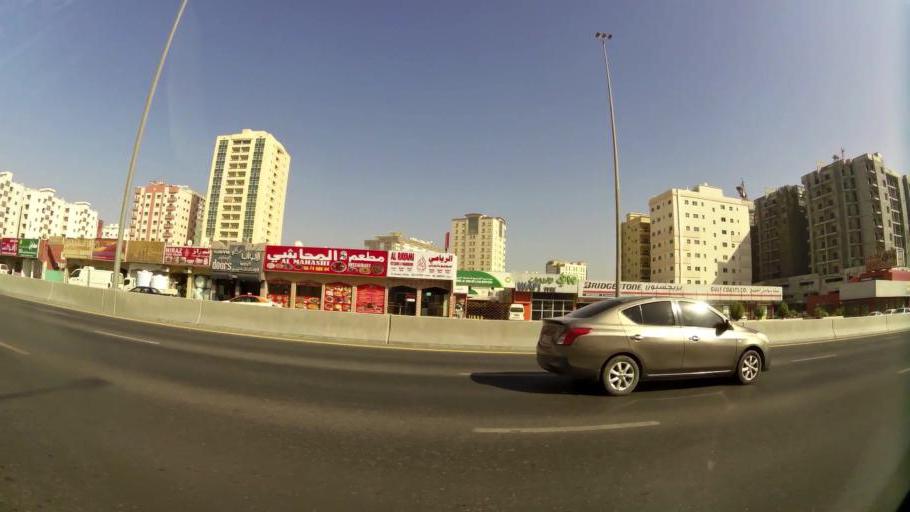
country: AE
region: Ajman
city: Ajman
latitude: 25.3880
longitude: 55.4689
